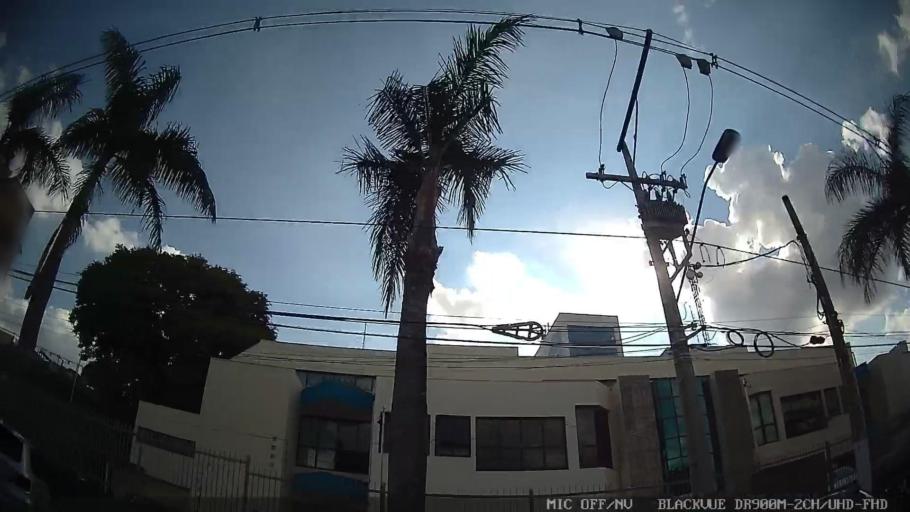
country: BR
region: Sao Paulo
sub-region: Braganca Paulista
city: Braganca Paulista
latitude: -22.9723
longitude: -46.5368
